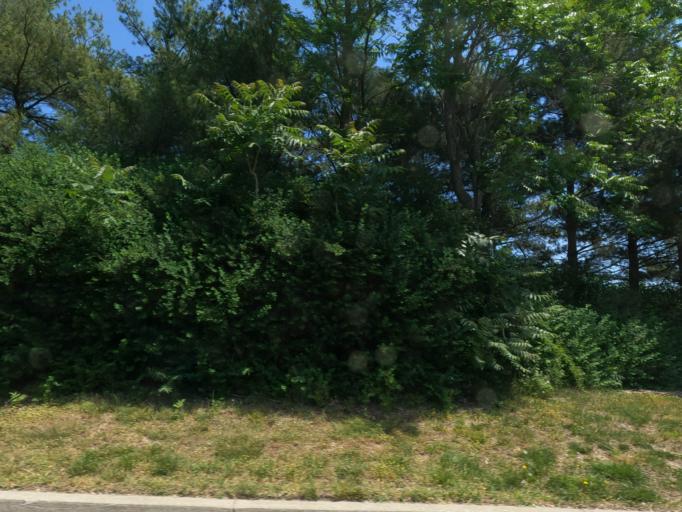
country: US
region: Maryland
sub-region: Howard County
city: Savage
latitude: 39.1755
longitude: -76.8118
